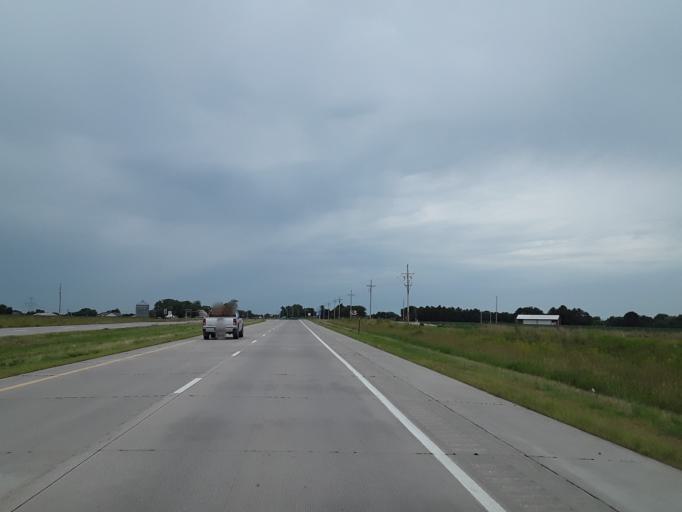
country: US
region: Nebraska
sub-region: Douglas County
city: Bennington
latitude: 41.4301
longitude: -96.1210
